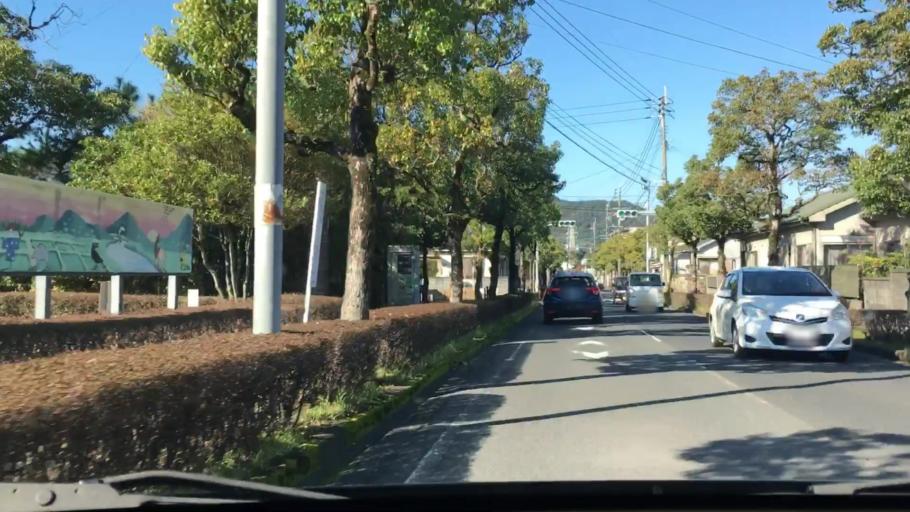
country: JP
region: Kagoshima
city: Kajiki
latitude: 31.7409
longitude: 130.6615
